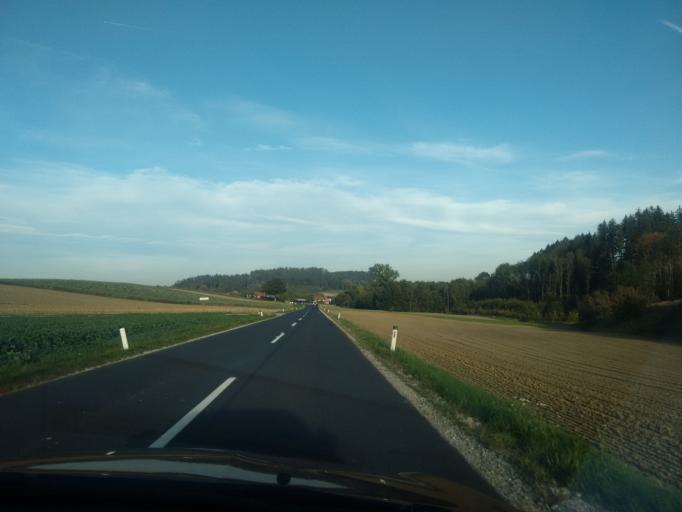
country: AT
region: Upper Austria
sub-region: Politischer Bezirk Vocklabruck
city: Niederthalheim
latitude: 48.1283
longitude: 13.7159
